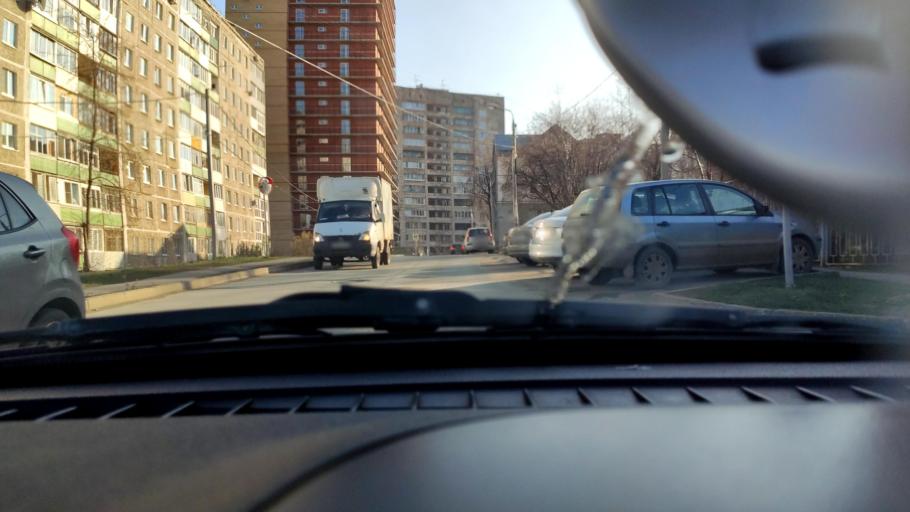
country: RU
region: Perm
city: Perm
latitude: 58.0304
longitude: 56.3102
